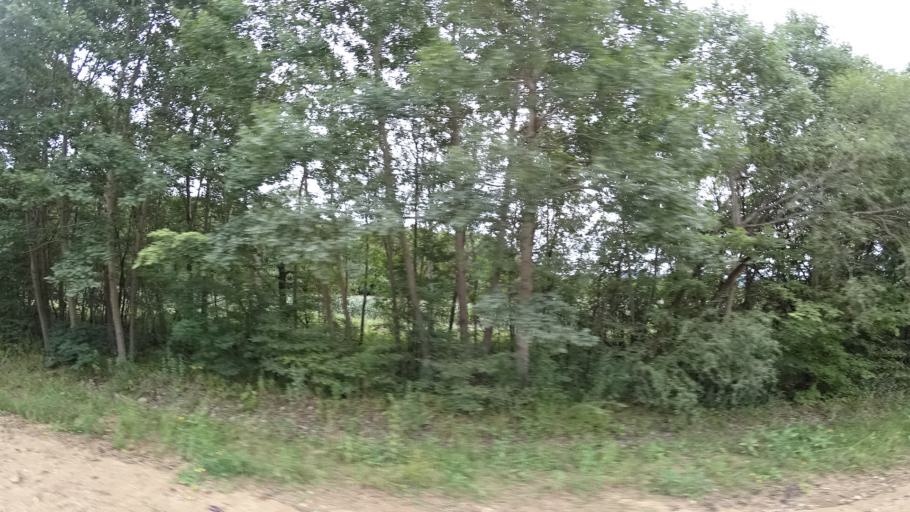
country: RU
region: Primorskiy
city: Rettikhovka
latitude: 44.1574
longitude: 132.6849
